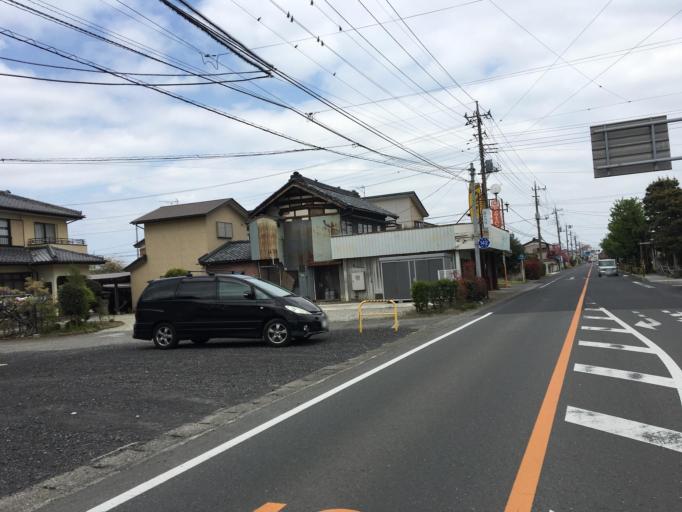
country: JP
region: Gunma
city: Isesaki
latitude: 36.2913
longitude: 139.1674
